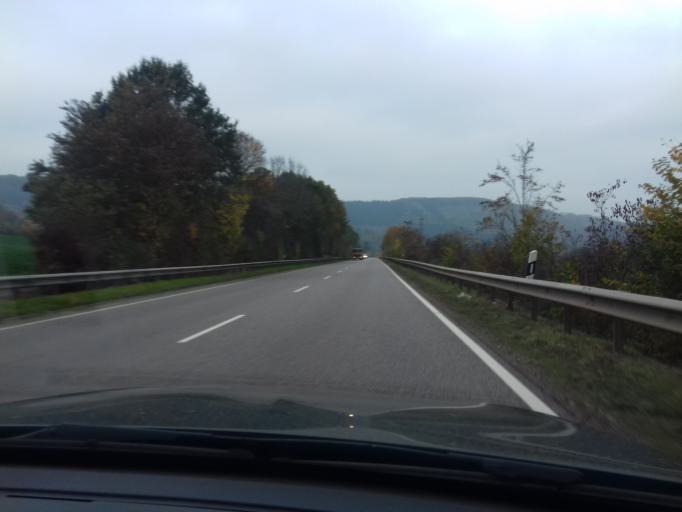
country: DE
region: Rheinland-Pfalz
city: Ayl
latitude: 49.6394
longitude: 6.5458
